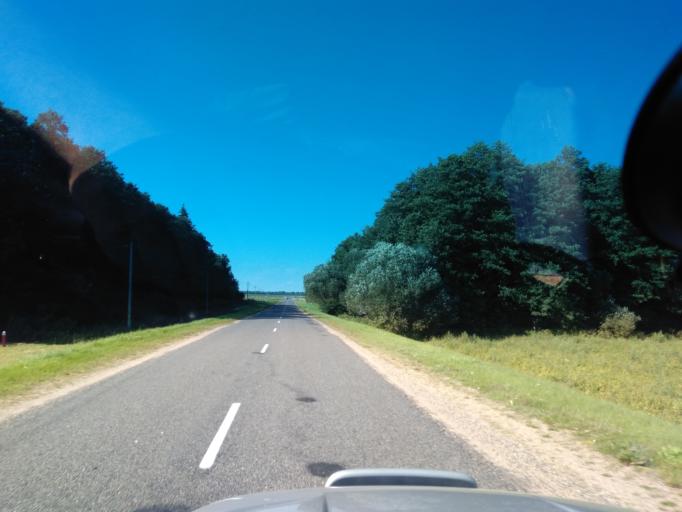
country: BY
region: Minsk
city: Kapyl'
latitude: 53.2353
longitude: 27.1005
